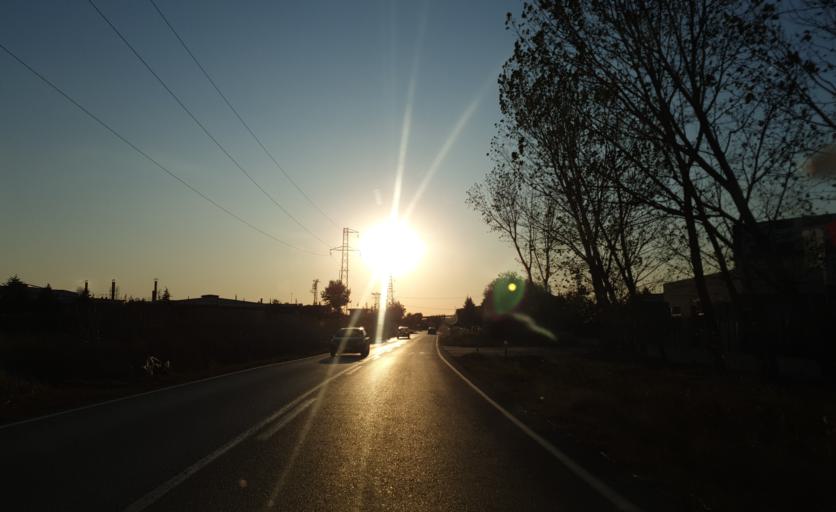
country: TR
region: Tekirdag
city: Beyazkoy
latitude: 41.3368
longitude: 27.7035
